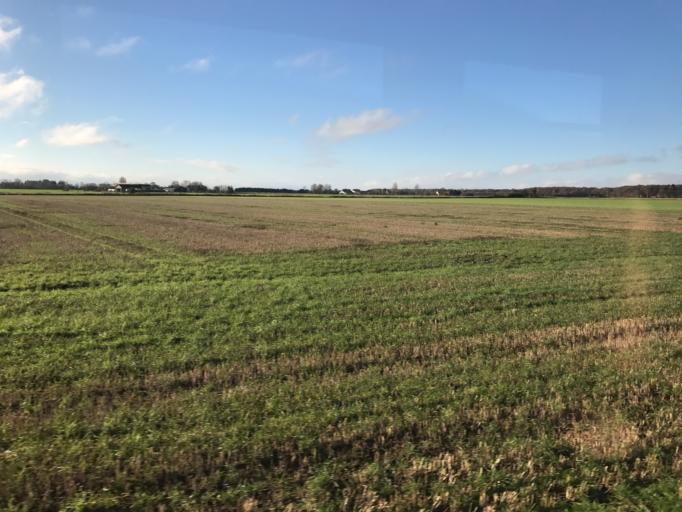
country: DK
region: Zealand
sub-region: Stevns Kommune
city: Store Heddinge
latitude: 55.3174
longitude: 12.3760
